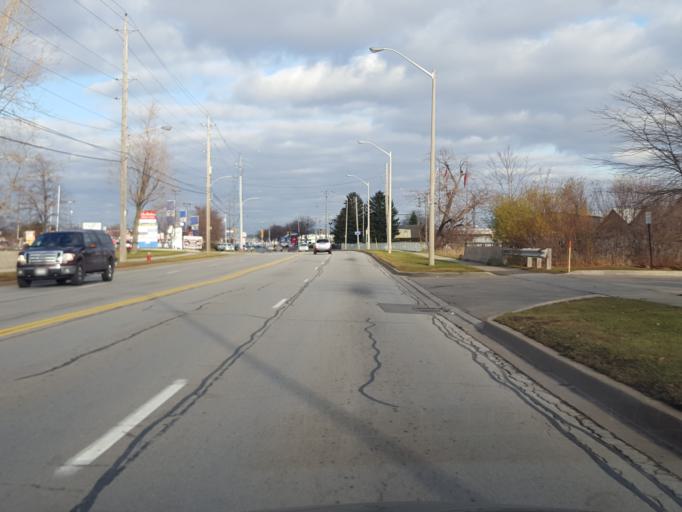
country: CA
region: Ontario
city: Burlington
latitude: 43.3611
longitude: -79.7861
